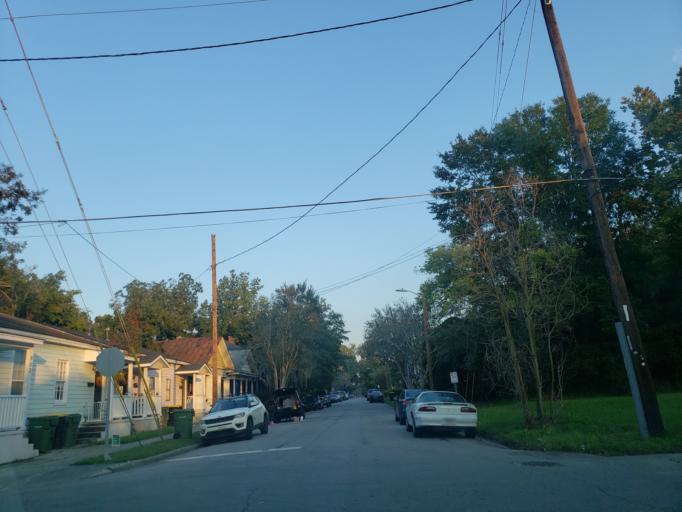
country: US
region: Georgia
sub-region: Chatham County
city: Savannah
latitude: 32.0631
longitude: -81.0840
